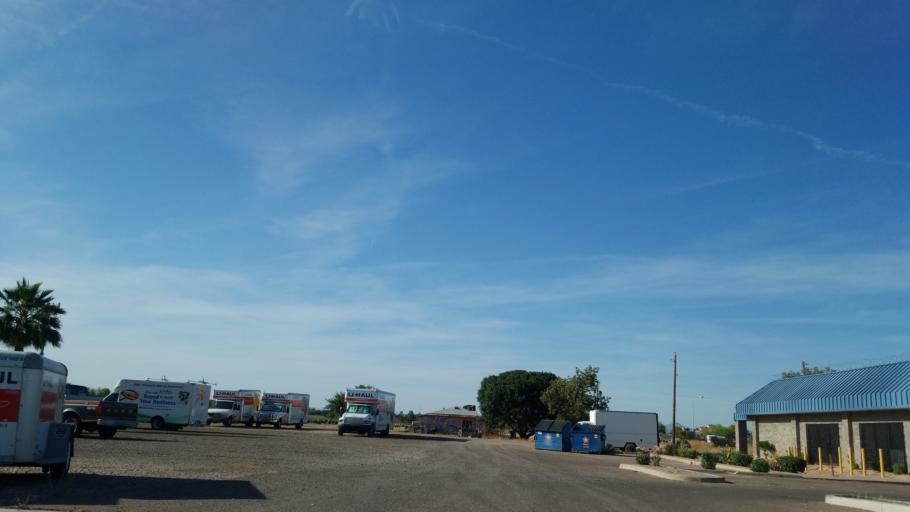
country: US
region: Arizona
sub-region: Maricopa County
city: Queen Creek
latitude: 33.3073
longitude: -111.6899
